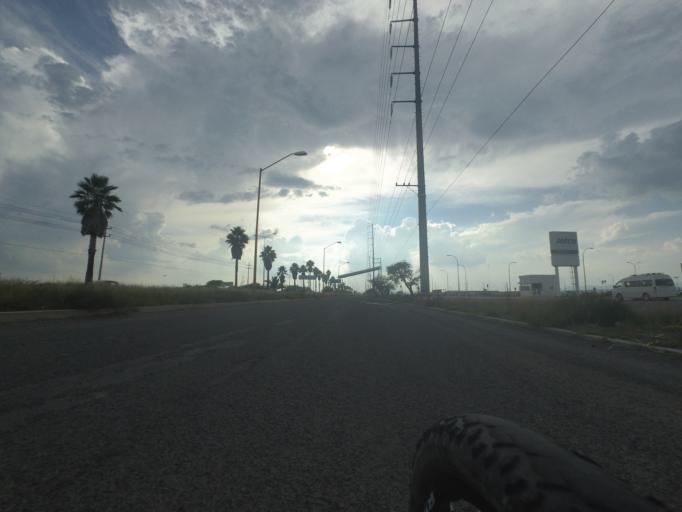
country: MX
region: Aguascalientes
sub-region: Aguascalientes
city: Penuelas (El Cienegal)
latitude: 21.7253
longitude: -102.2973
